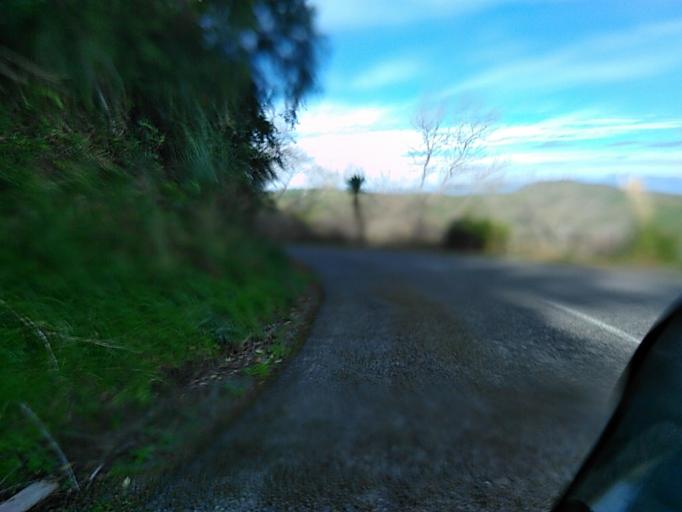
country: NZ
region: Gisborne
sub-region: Gisborne District
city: Gisborne
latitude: -38.6392
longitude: 178.0580
